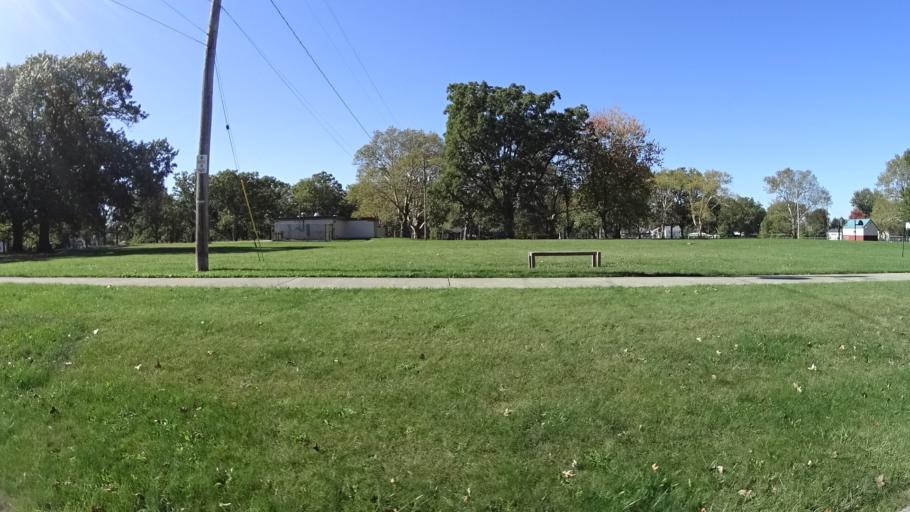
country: US
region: Ohio
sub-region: Lorain County
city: Lorain
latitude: 41.4442
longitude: -82.1717
